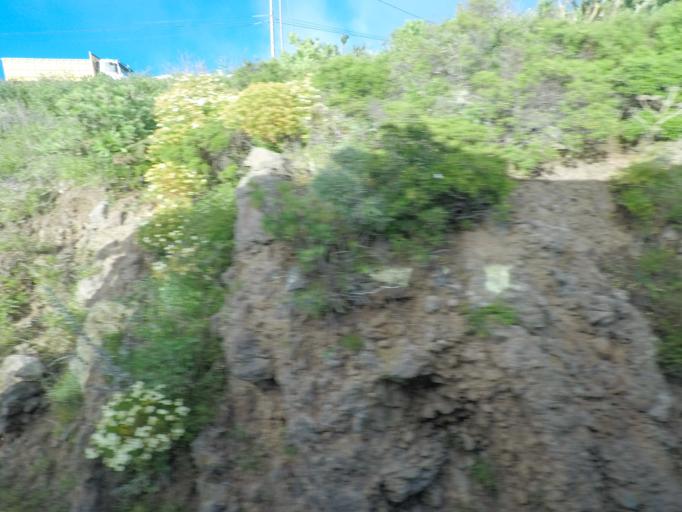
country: ES
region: Canary Islands
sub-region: Provincia de Santa Cruz de Tenerife
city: Alajero
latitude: 28.0983
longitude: -17.1824
